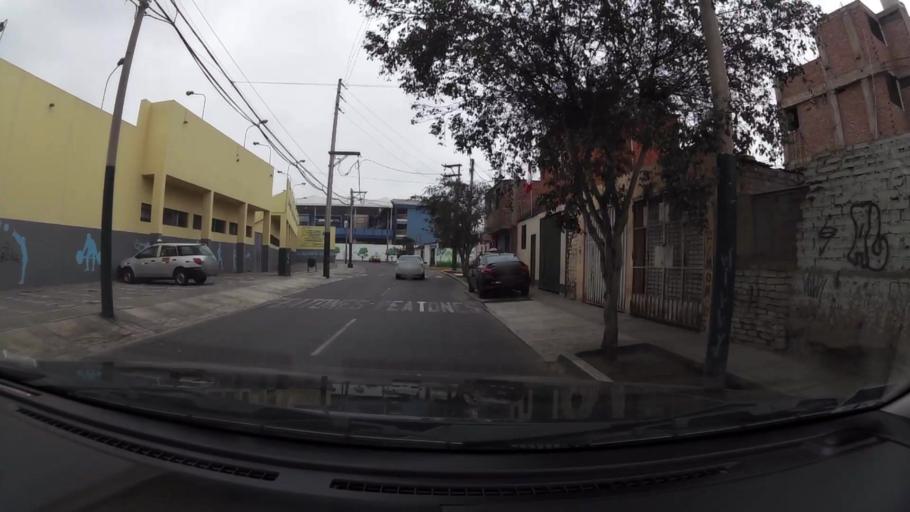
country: PE
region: Lima
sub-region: Lima
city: Surco
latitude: -12.1460
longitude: -77.0010
